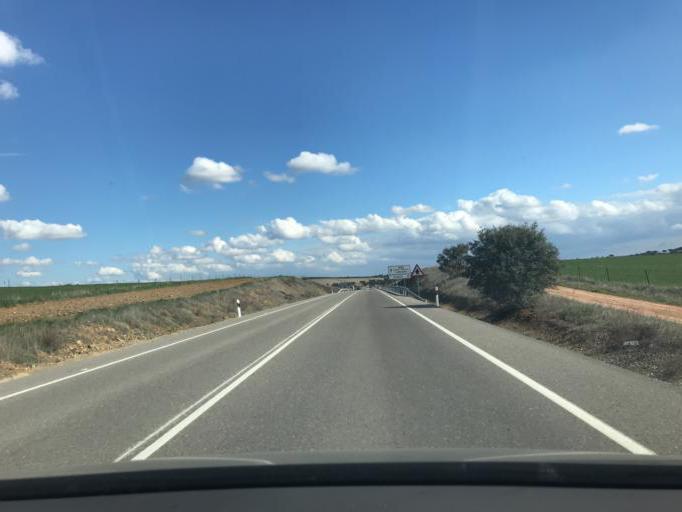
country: ES
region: Extremadura
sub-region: Provincia de Badajoz
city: Granja de Torrehermosa
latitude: 38.2898
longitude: -5.5306
